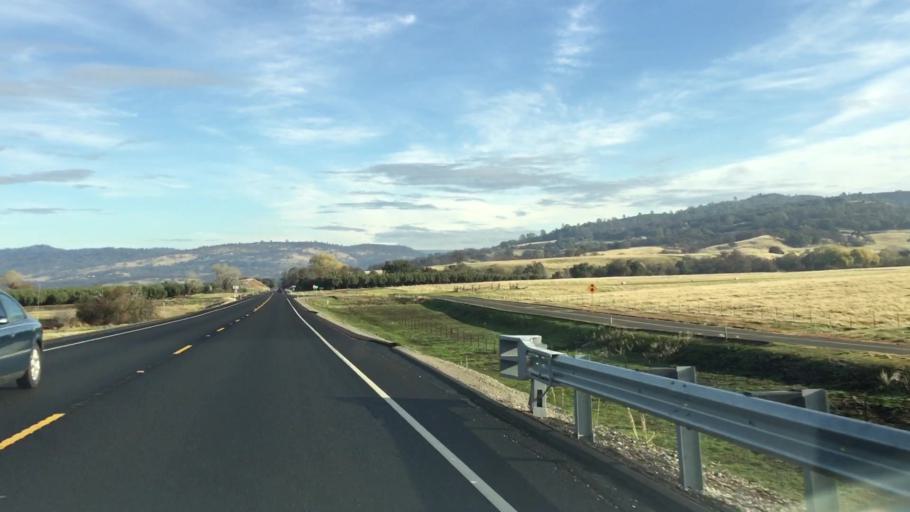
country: US
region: California
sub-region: Butte County
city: Thermalito
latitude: 39.6233
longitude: -121.5955
